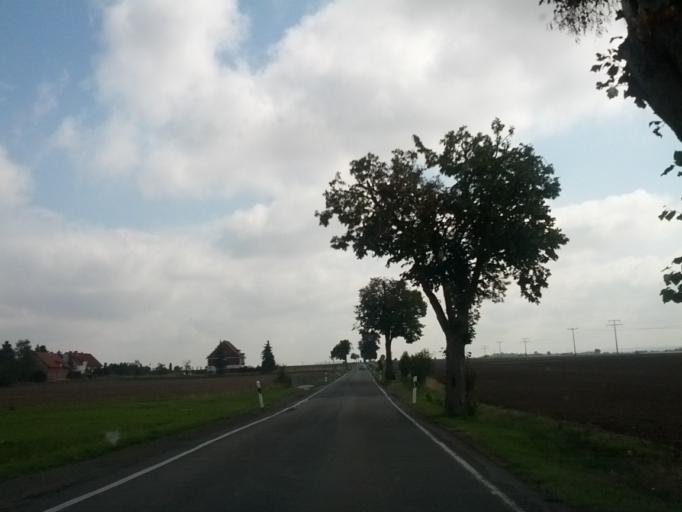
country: DE
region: Thuringia
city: Schwabhausen
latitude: 50.9205
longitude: 10.7324
